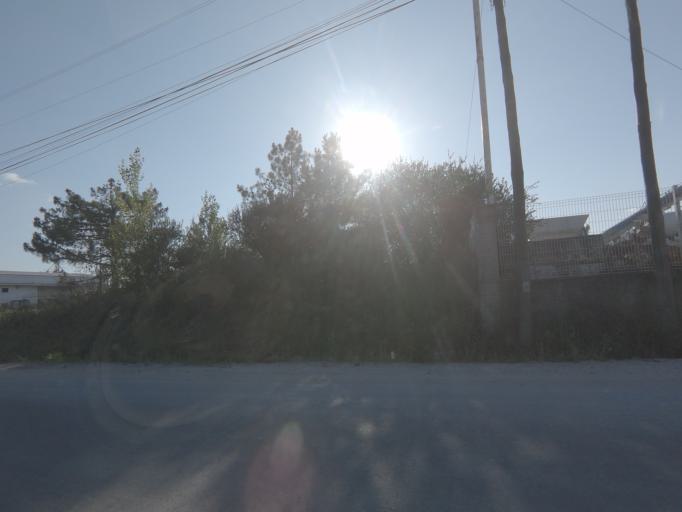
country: PT
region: Vila Real
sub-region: Chaves
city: Chaves
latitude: 41.7887
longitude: -7.4338
